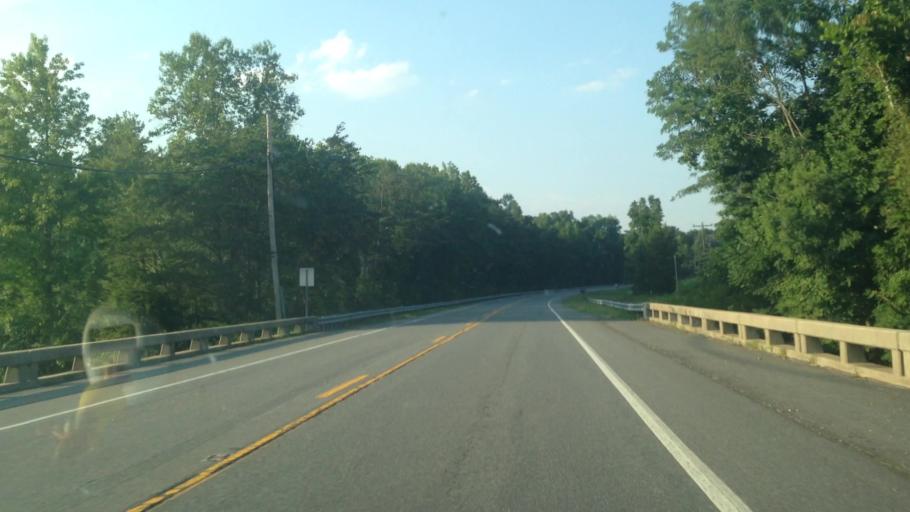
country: US
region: North Carolina
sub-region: Rockingham County
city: Reidsville
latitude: 36.3061
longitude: -79.7213
